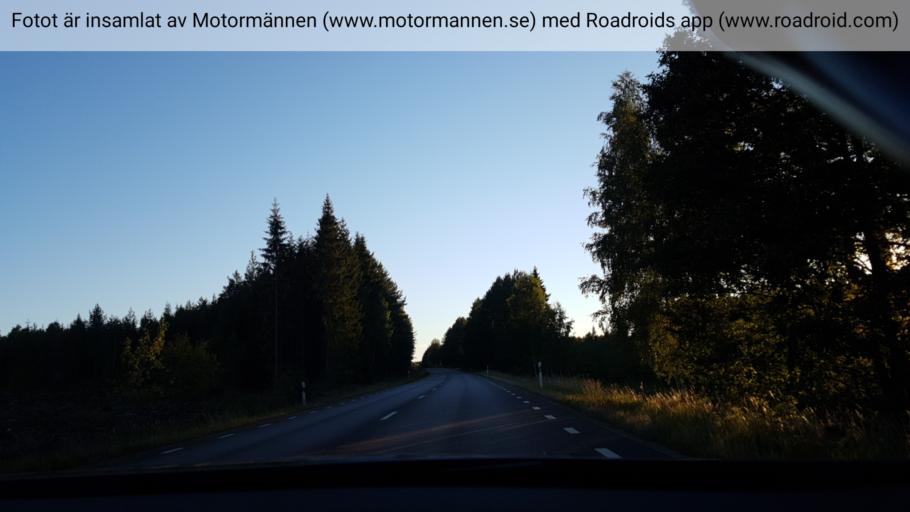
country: SE
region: Vaestra Goetaland
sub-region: Hjo Kommun
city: Hjo
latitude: 58.3414
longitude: 14.2155
